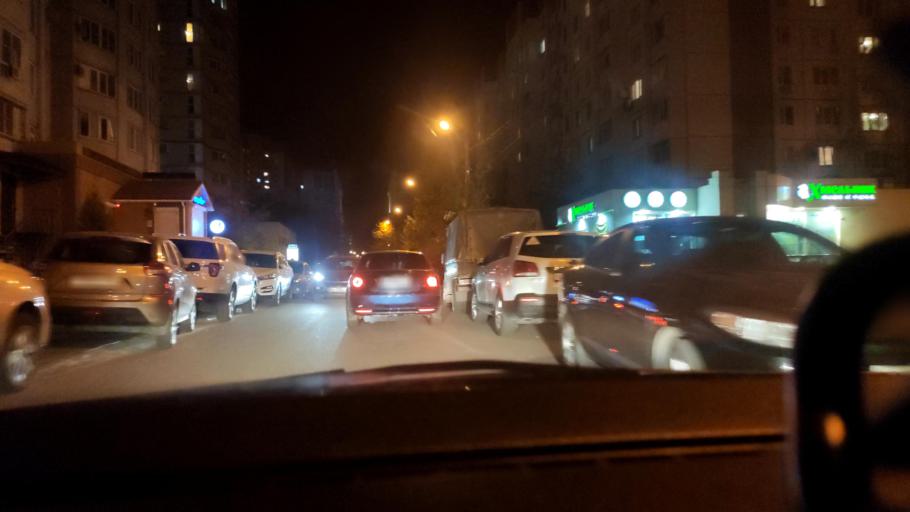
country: RU
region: Voronezj
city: Voronezh
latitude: 51.7111
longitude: 39.1869
